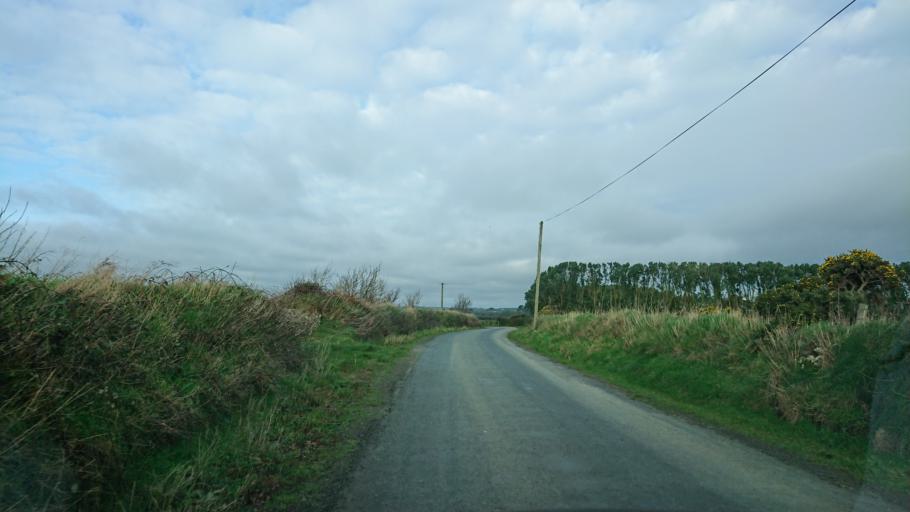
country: IE
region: Munster
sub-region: Waterford
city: Portlaw
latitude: 52.1438
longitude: -7.3052
